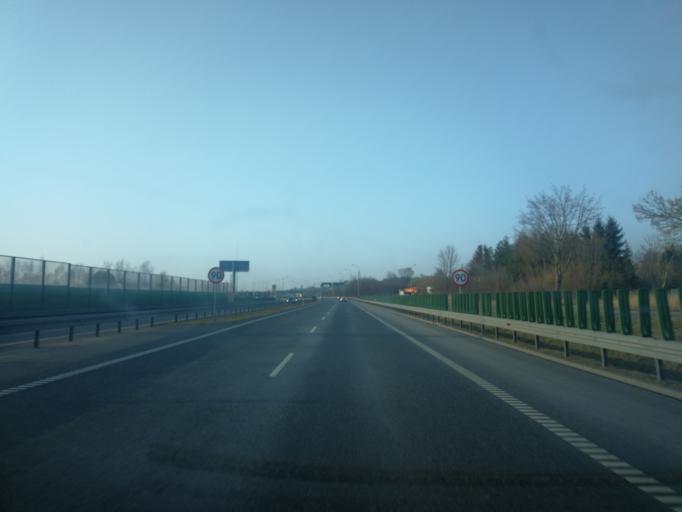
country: PL
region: Warmian-Masurian Voivodeship
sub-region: Powiat elblaski
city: Gronowo Gorne
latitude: 54.1337
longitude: 19.4559
